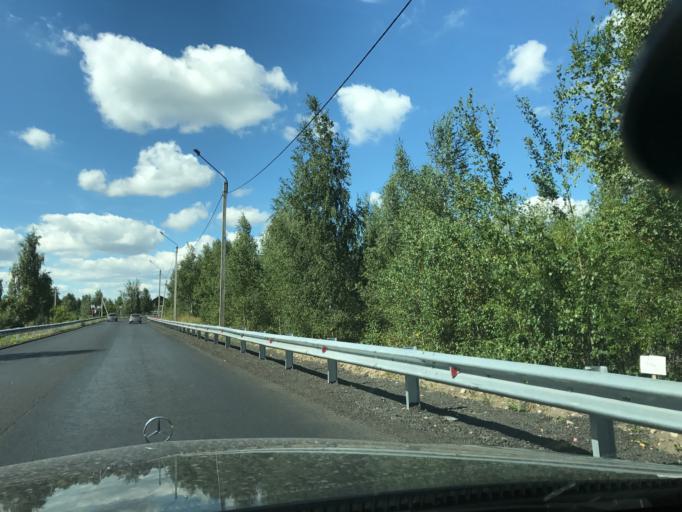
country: RU
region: Nizjnij Novgorod
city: Gorbatovka
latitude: 56.2202
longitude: 43.7477
